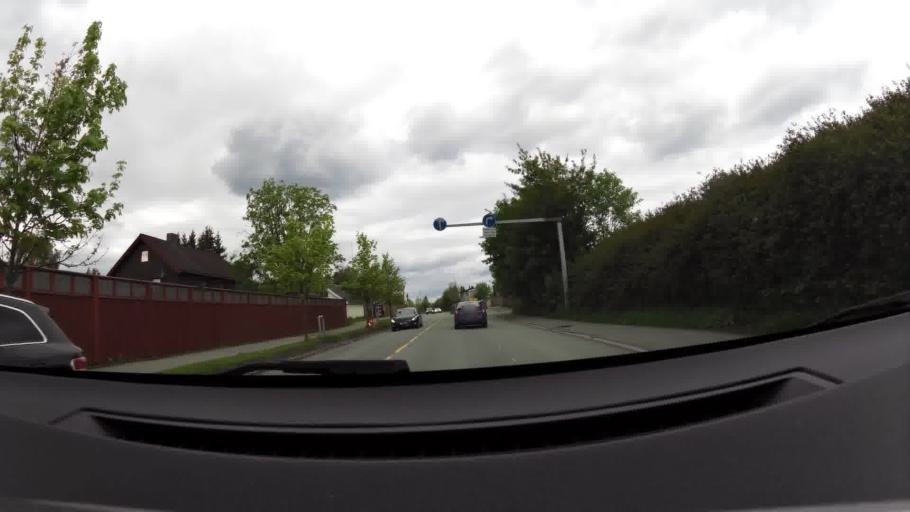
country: NO
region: Sor-Trondelag
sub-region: Trondheim
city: Trondheim
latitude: 63.4058
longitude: 10.4256
